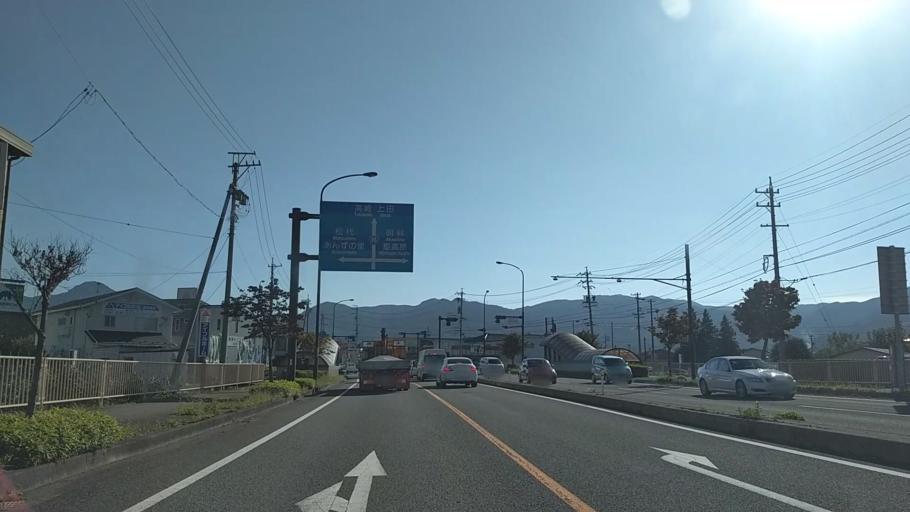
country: JP
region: Nagano
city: Nagano-shi
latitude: 36.5418
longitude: 138.1235
